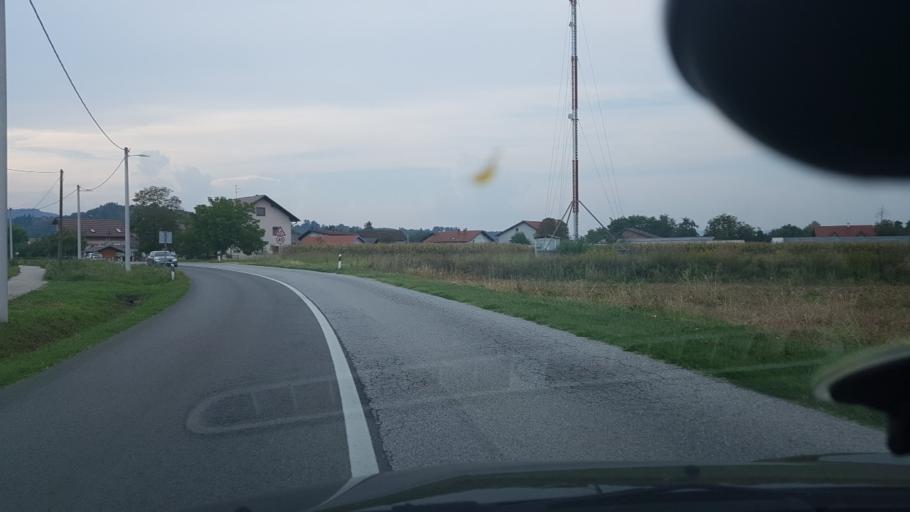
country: HR
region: Zagrebacka
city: Bregana
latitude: 45.8394
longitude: 15.6944
